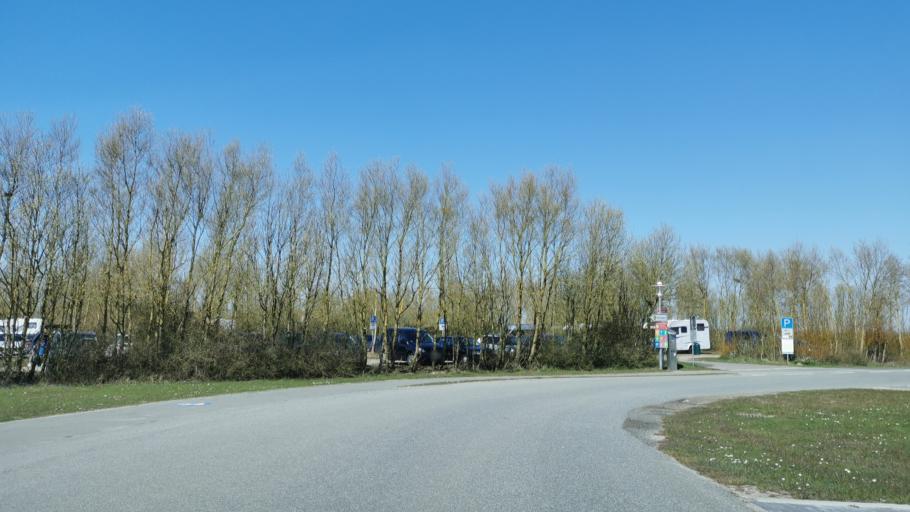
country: DE
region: Schleswig-Holstein
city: Busum
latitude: 54.1412
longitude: 8.8441
